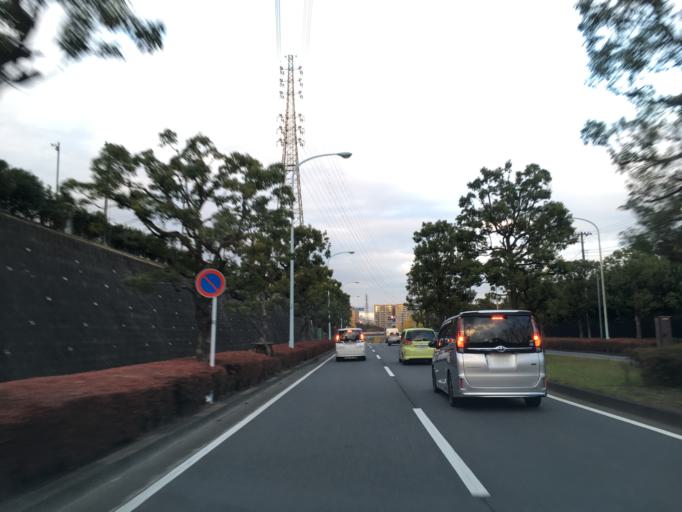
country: JP
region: Tokyo
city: Hachioji
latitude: 35.6080
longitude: 139.3707
